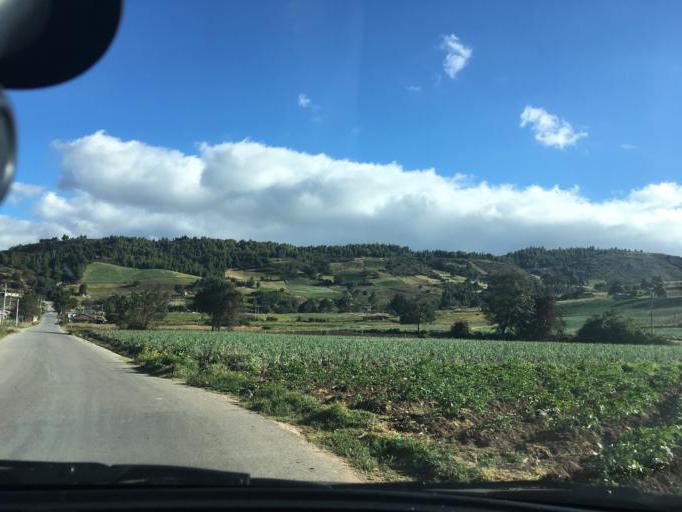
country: CO
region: Boyaca
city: Pesca
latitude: 5.5142
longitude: -72.9763
